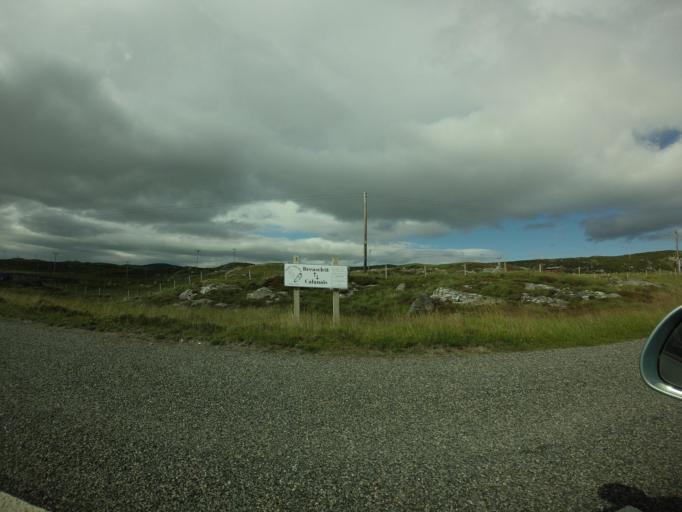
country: GB
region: Scotland
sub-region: Eilean Siar
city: Harris
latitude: 58.1977
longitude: -6.7257
